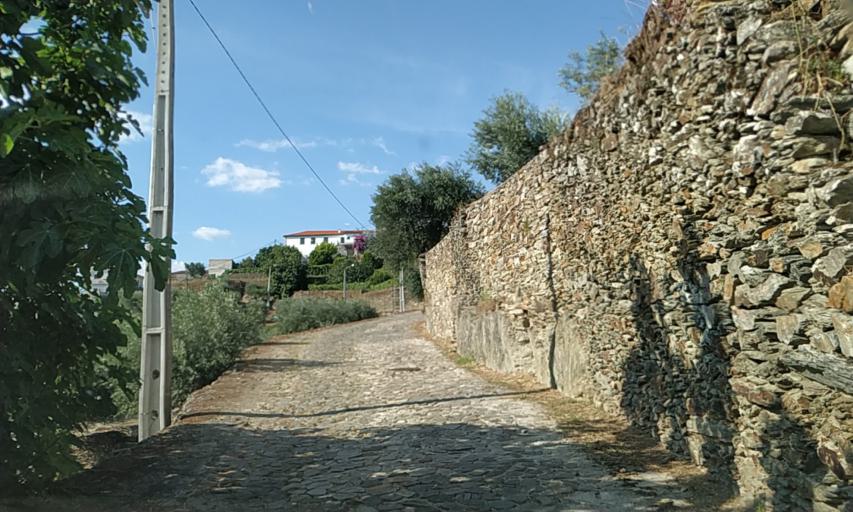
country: PT
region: Vila Real
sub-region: Sabrosa
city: Vilela
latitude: 41.1992
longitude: -7.5357
